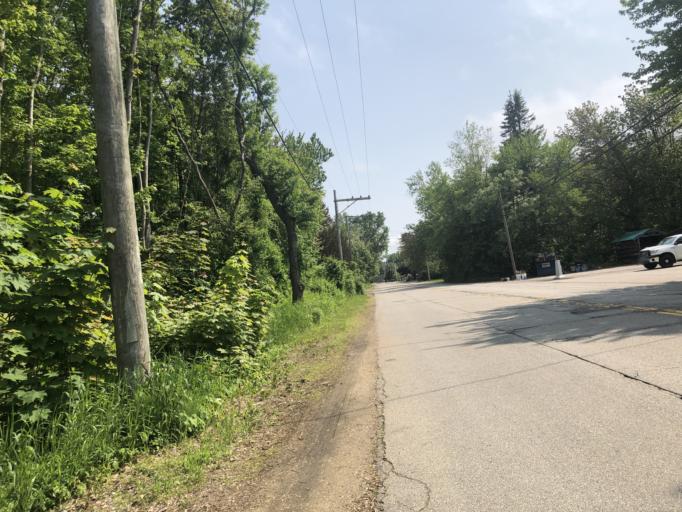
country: US
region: Maine
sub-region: York County
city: Eliot
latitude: 43.1315
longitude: -70.8360
